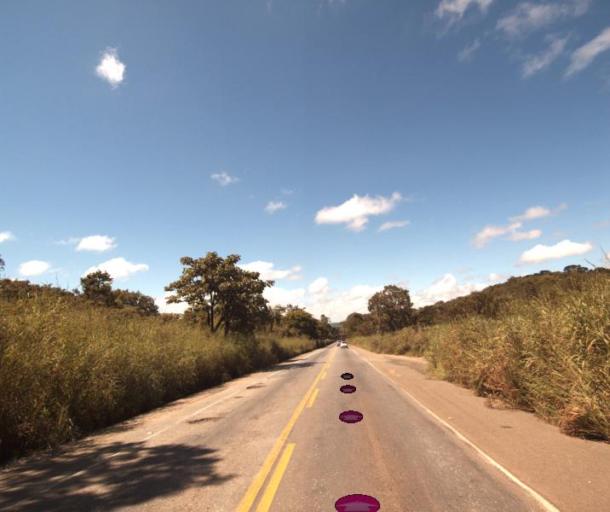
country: BR
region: Goias
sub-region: Jaragua
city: Jaragua
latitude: -15.6976
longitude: -49.3353
